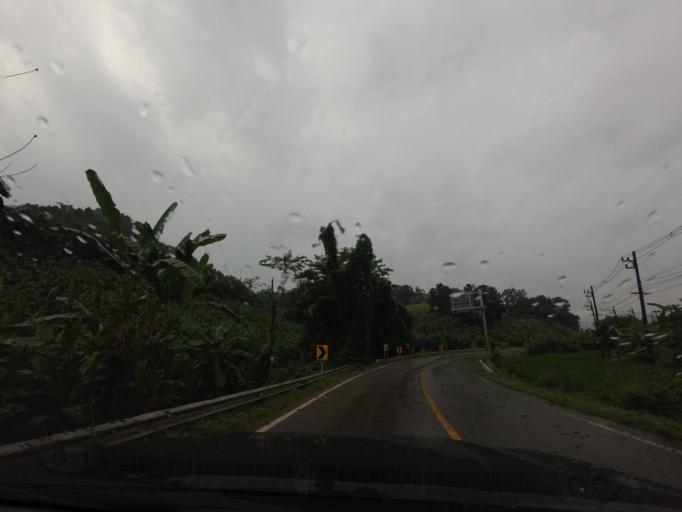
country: TH
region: Nong Khai
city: Sangkhom
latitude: 18.2076
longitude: 102.1029
